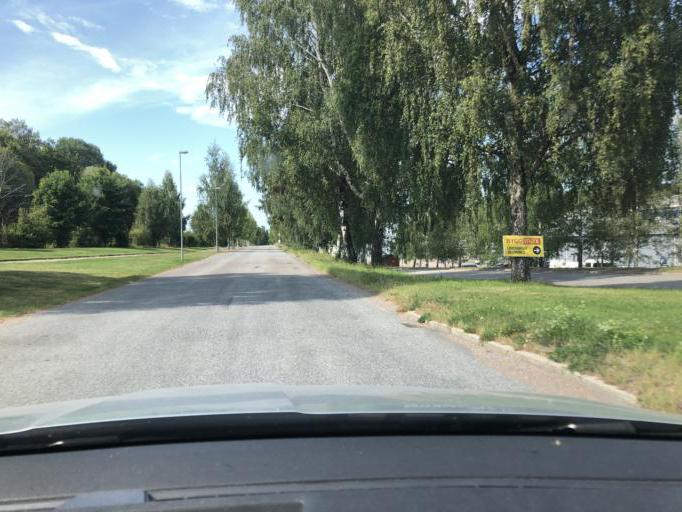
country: SE
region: Dalarna
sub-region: Avesta Kommun
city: Avesta
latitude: 60.1458
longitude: 16.1912
